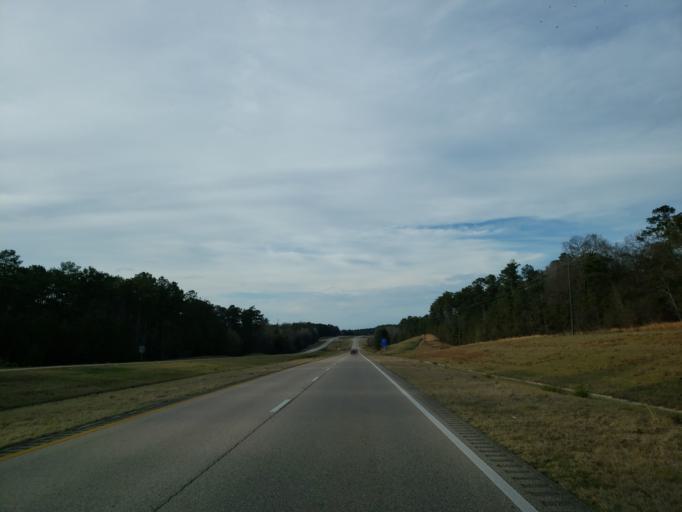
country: US
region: Mississippi
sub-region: Wayne County
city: Waynesboro
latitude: 31.6210
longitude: -88.5810
